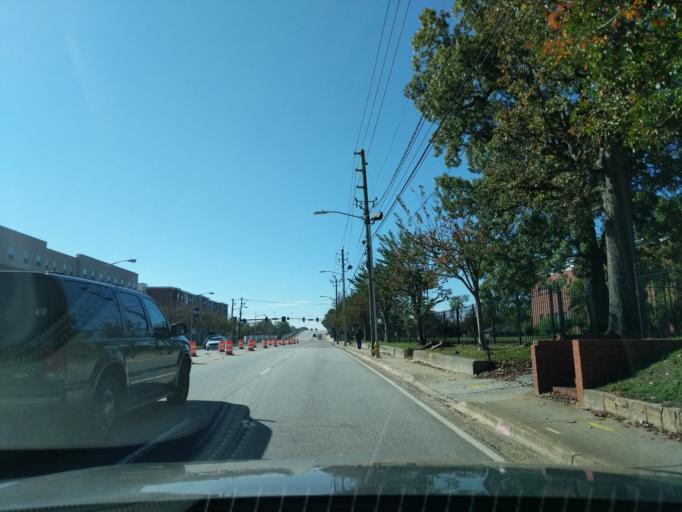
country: US
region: Georgia
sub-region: Richmond County
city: Augusta
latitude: 33.4685
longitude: -81.9927
